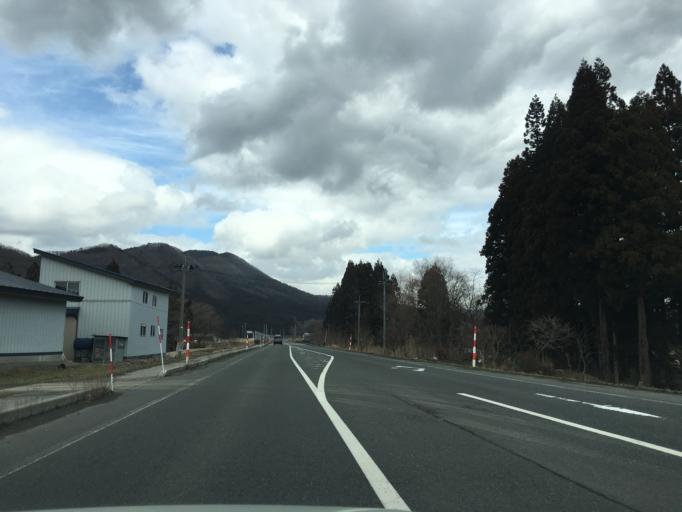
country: JP
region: Akita
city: Hanawa
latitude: 40.2249
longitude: 140.6779
